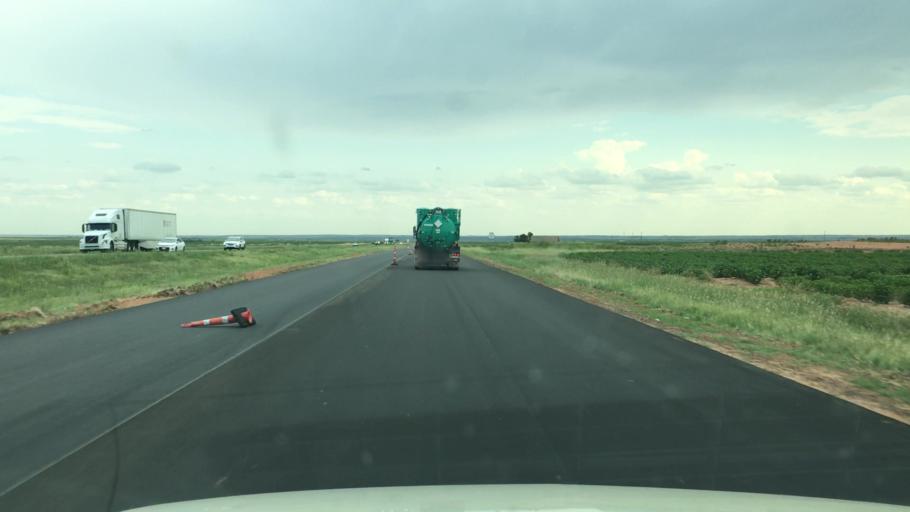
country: US
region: Texas
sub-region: Hall County
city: Memphis
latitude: 34.6242
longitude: -100.4737
